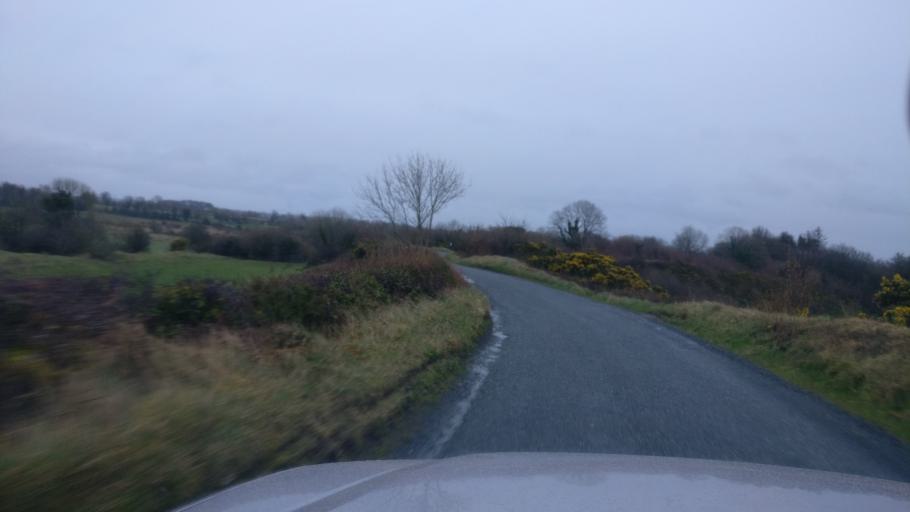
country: IE
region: Connaught
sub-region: County Galway
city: Ballinasloe
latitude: 53.2986
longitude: -8.2669
